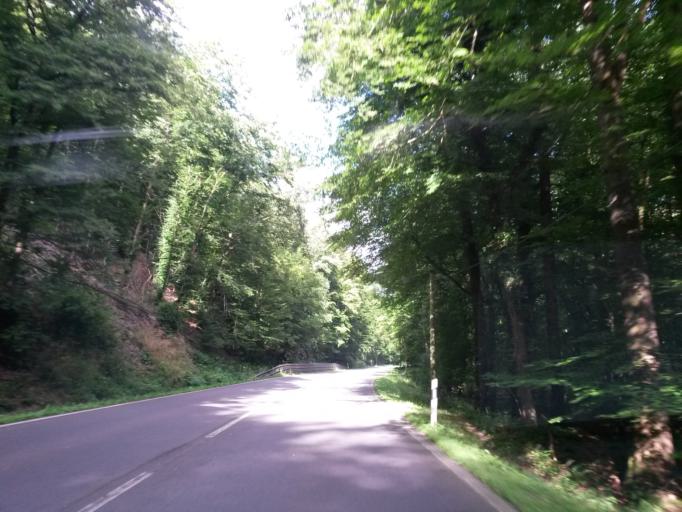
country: DE
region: North Rhine-Westphalia
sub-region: Regierungsbezirk Koln
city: Much
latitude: 50.8245
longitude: 7.3691
